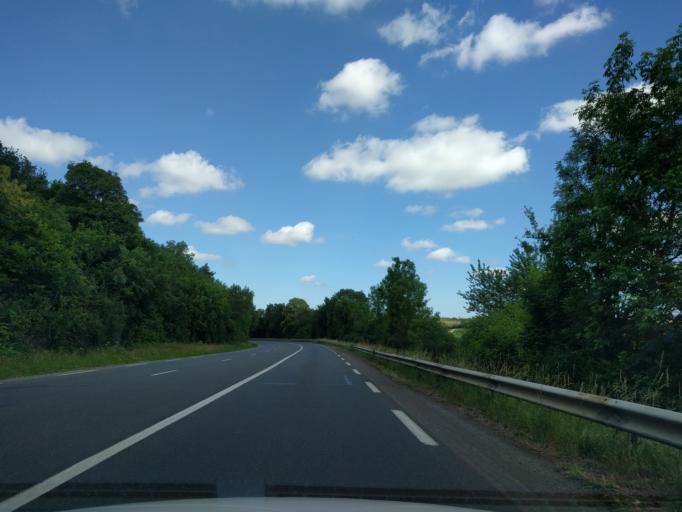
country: FR
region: Pays de la Loire
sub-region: Departement de la Vendee
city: Chantonnay
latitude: 46.6526
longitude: -1.0388
